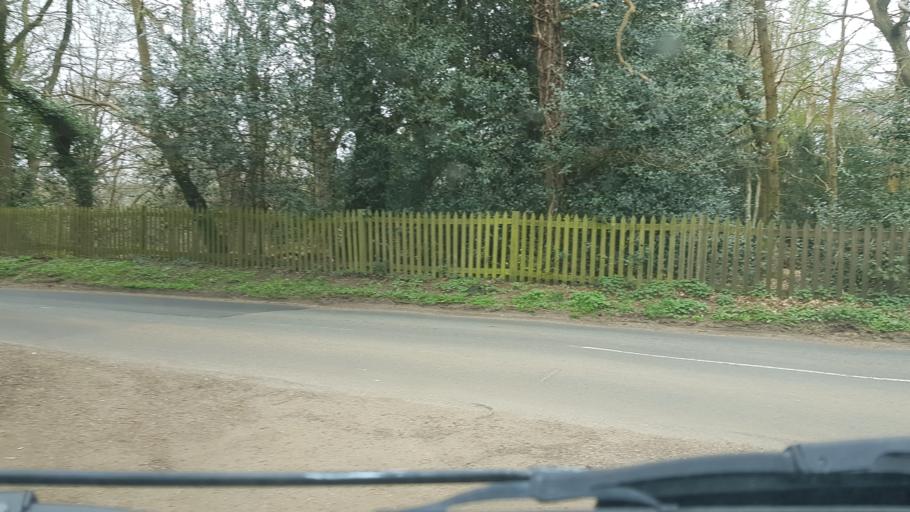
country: GB
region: England
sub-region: Surrey
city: Chilworth
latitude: 51.2143
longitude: -0.4848
